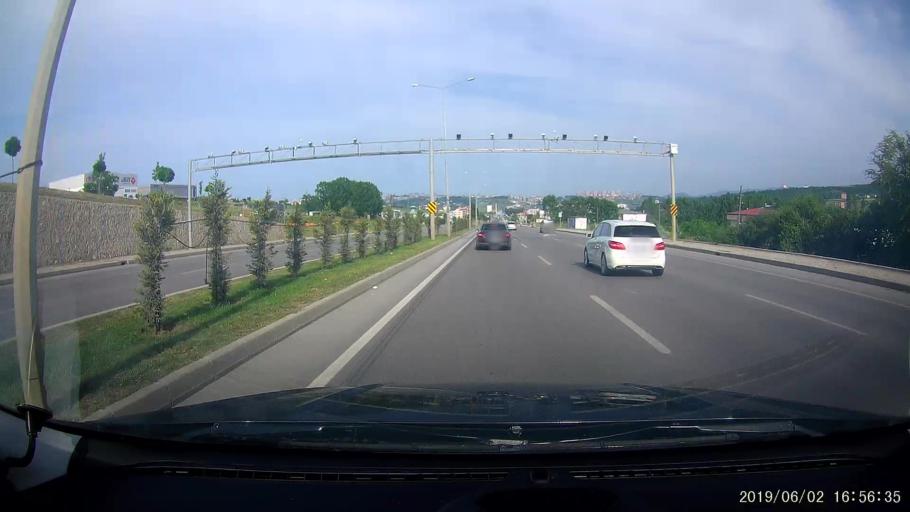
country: TR
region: Samsun
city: Samsun
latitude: 41.2925
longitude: 36.2626
